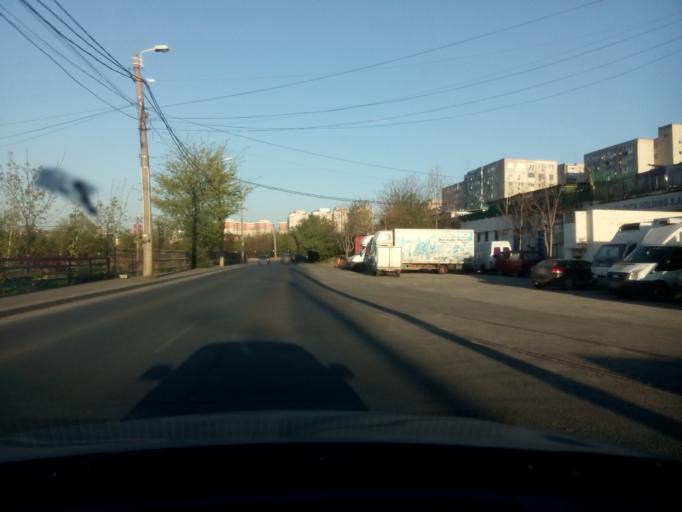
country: RO
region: Ilfov
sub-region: Comuna Fundeni-Dobroesti
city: Fundeni
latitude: 44.4454
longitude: 26.1583
